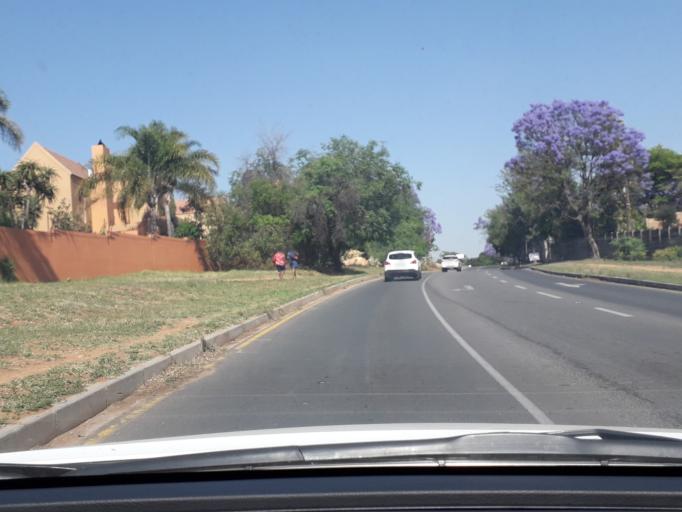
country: ZA
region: Gauteng
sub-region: City of Johannesburg Metropolitan Municipality
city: Roodepoort
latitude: -26.0833
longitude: 27.9570
